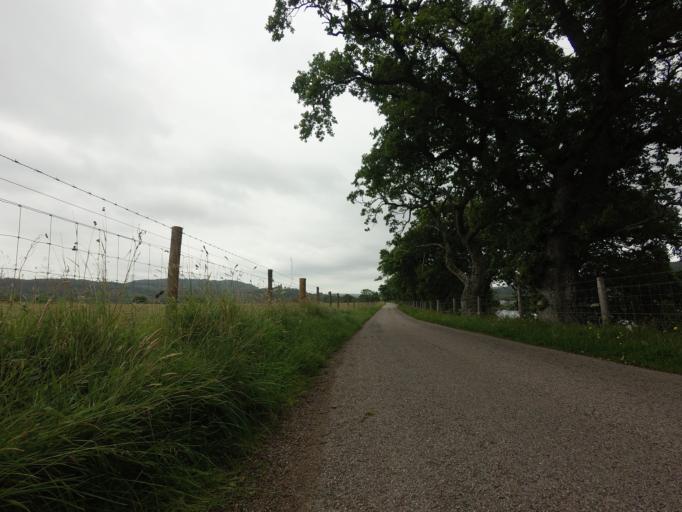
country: GB
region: Scotland
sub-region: Highland
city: Evanton
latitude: 57.9129
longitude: -4.3990
